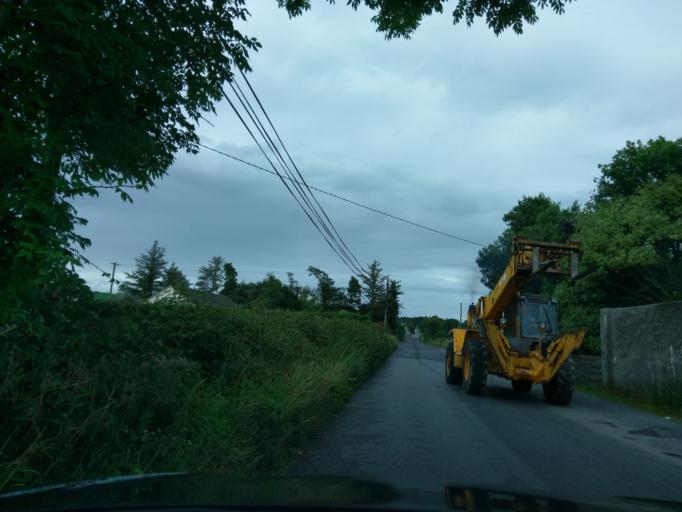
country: IE
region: Connaught
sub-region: County Galway
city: Gort
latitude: 53.1532
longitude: -8.7522
